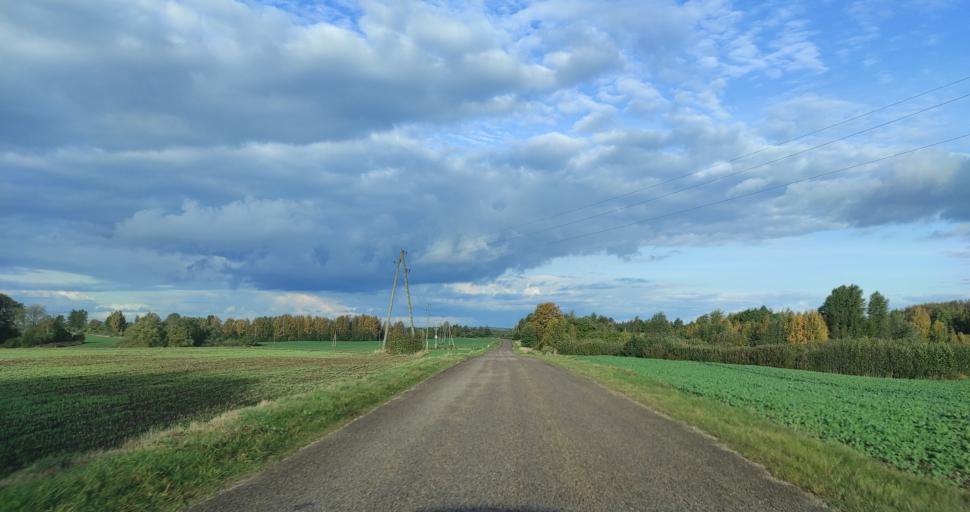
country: LV
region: Aizpute
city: Aizpute
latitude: 56.7764
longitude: 21.7808
